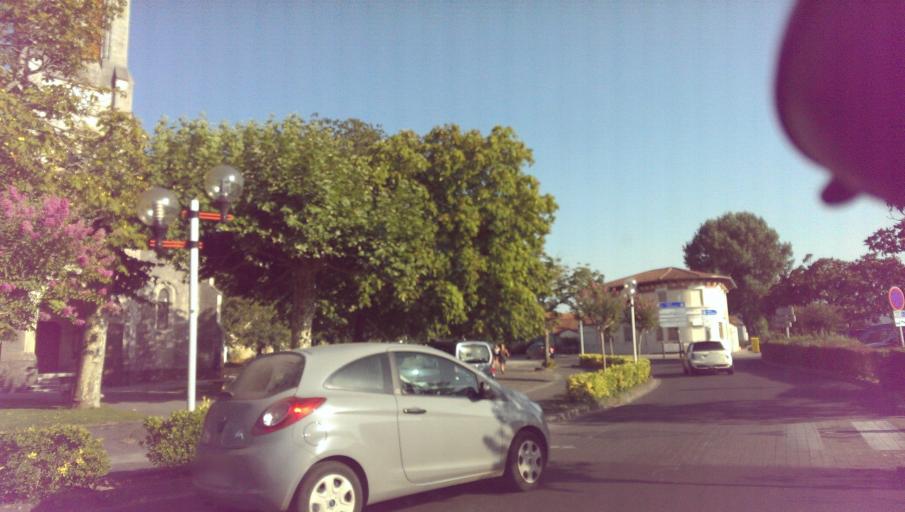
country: FR
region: Aquitaine
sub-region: Departement des Landes
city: Mimizan
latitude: 44.2025
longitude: -1.2296
